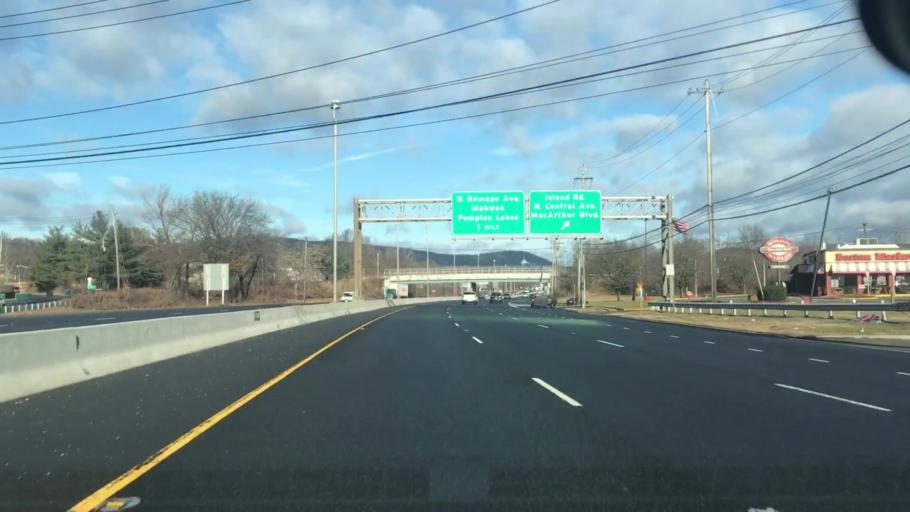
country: US
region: New Jersey
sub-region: Bergen County
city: Mahwah
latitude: 41.0790
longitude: -74.1491
